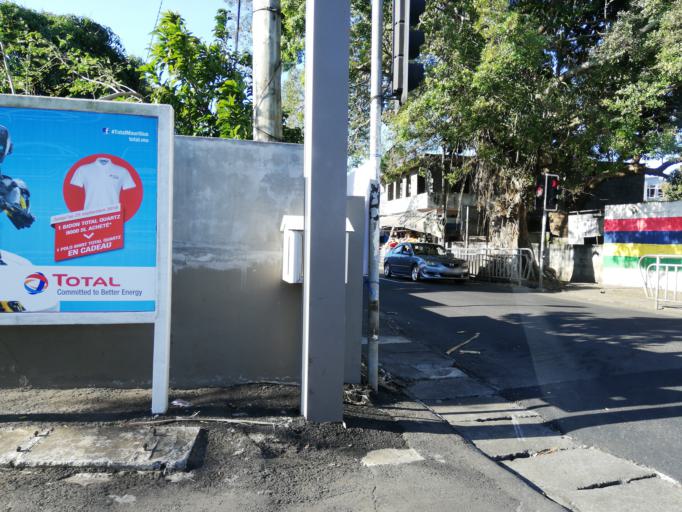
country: MU
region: Pamplemousses
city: Plaine des Papayes
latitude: -20.0632
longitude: 57.5806
